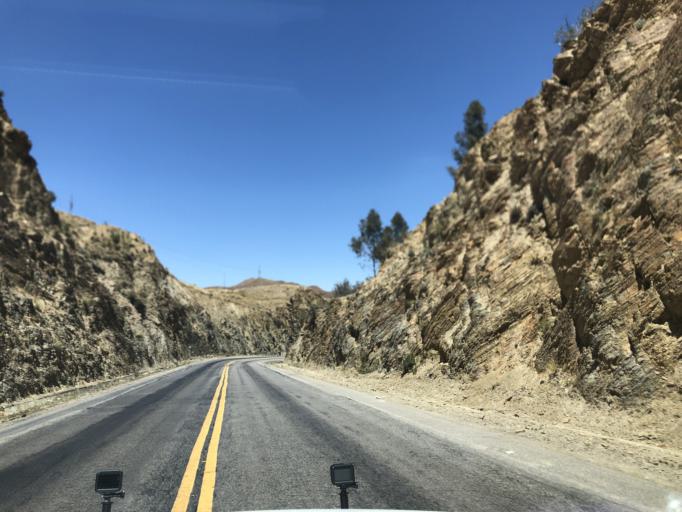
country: BO
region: Cochabamba
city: Sipe Sipe
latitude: -17.7146
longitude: -66.6298
